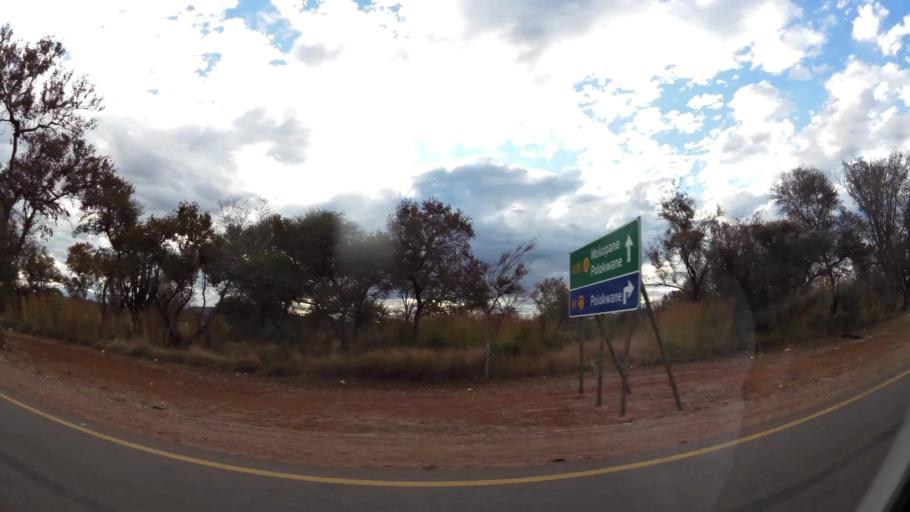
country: ZA
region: Limpopo
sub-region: Waterberg District Municipality
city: Modimolle
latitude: -24.5043
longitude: 28.7296
